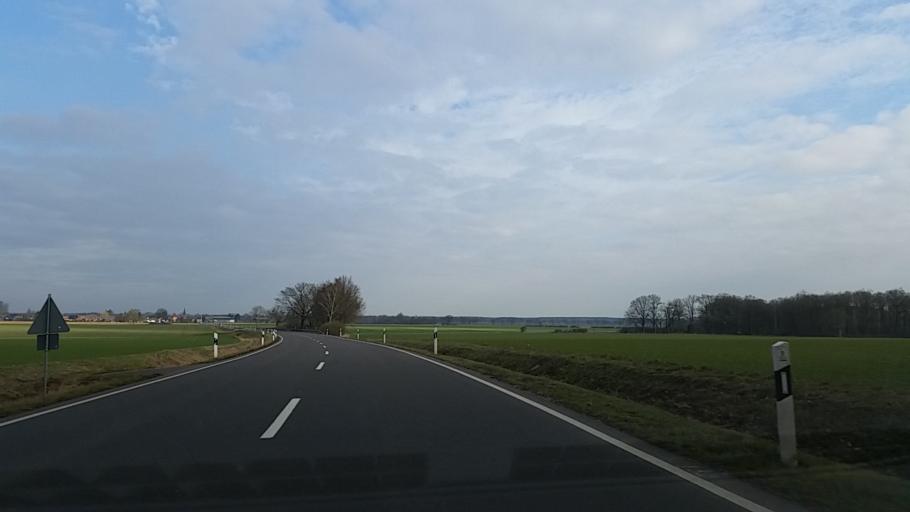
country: DE
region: Lower Saxony
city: Parsau
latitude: 52.5205
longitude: 10.8887
